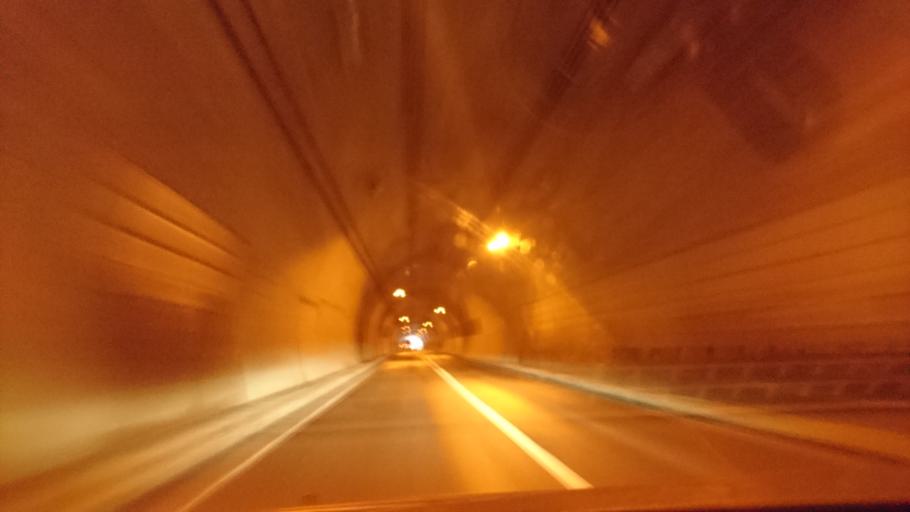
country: JP
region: Iwate
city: Ofunato
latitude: 39.0141
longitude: 141.4602
